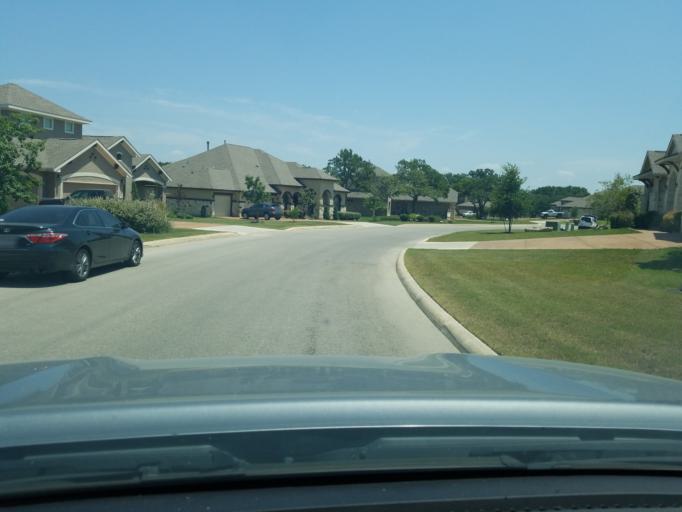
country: US
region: Texas
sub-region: Bexar County
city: Timberwood Park
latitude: 29.7099
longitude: -98.5120
